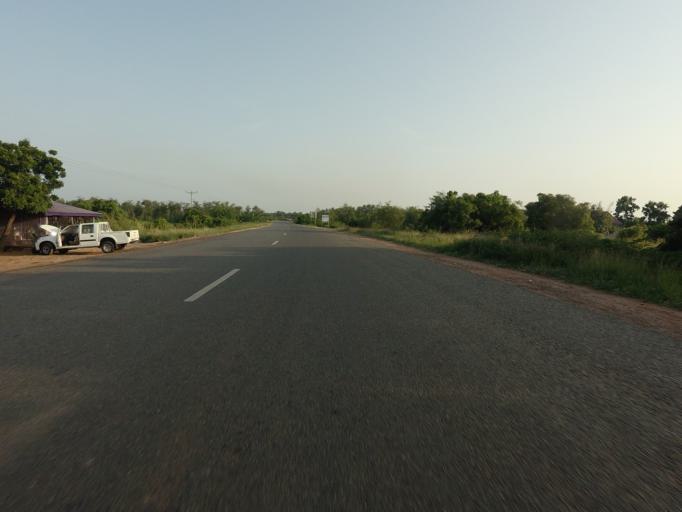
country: GH
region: Volta
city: Anloga
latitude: 5.9758
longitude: 0.6665
